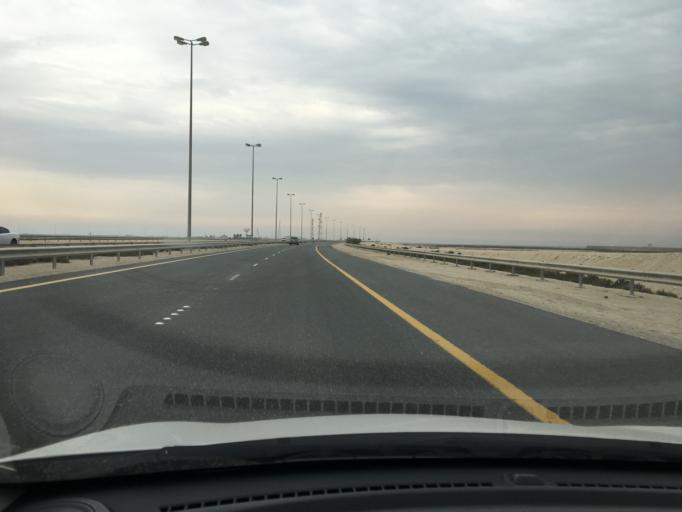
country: BH
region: Central Governorate
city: Dar Kulayb
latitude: 25.8574
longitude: 50.5851
